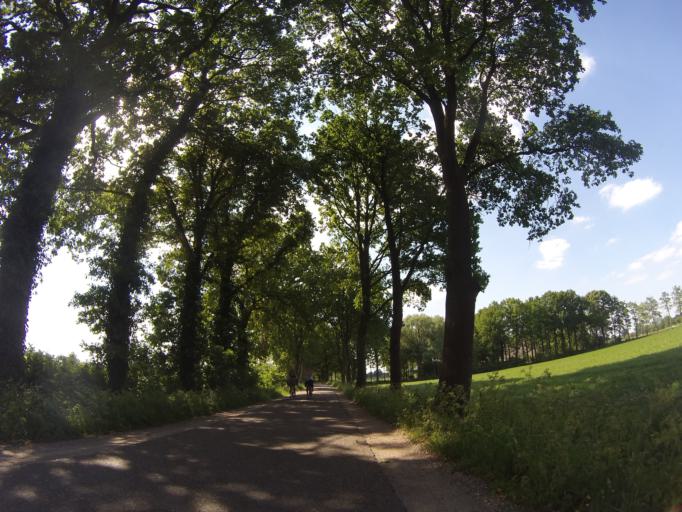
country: NL
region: Gelderland
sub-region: Gemeente Barneveld
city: Terschuur
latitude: 52.1465
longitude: 5.4862
